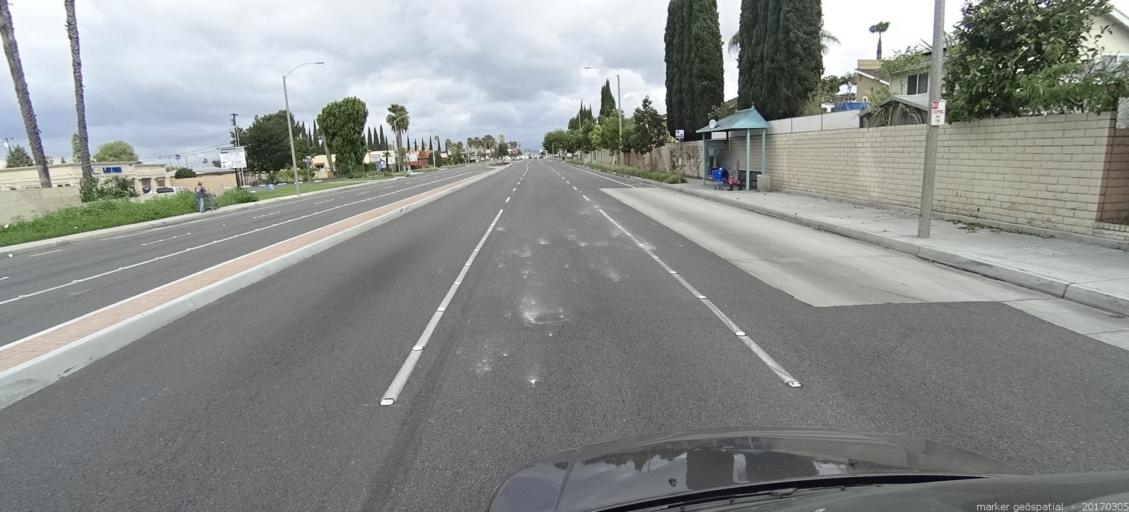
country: US
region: California
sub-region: Orange County
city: Stanton
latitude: 33.8140
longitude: -117.9589
